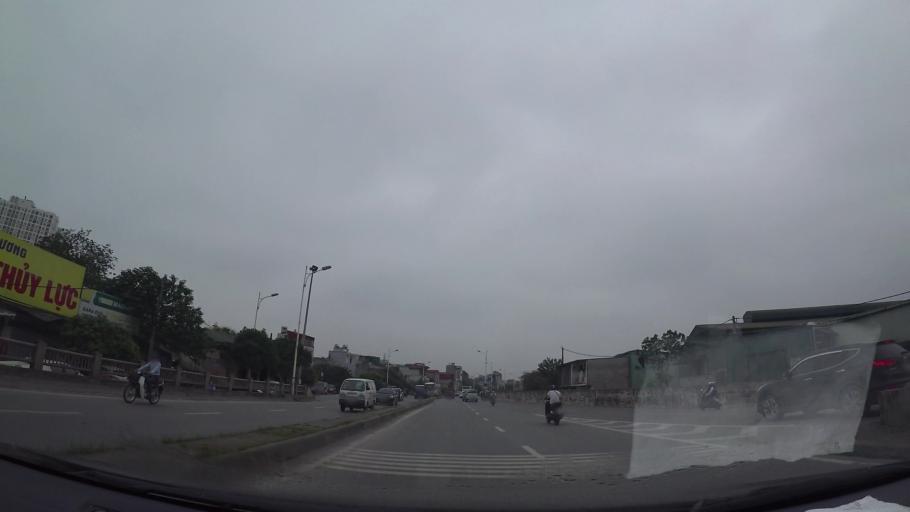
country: VN
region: Ha Noi
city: Hai BaTrung
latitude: 21.0031
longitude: 105.8726
